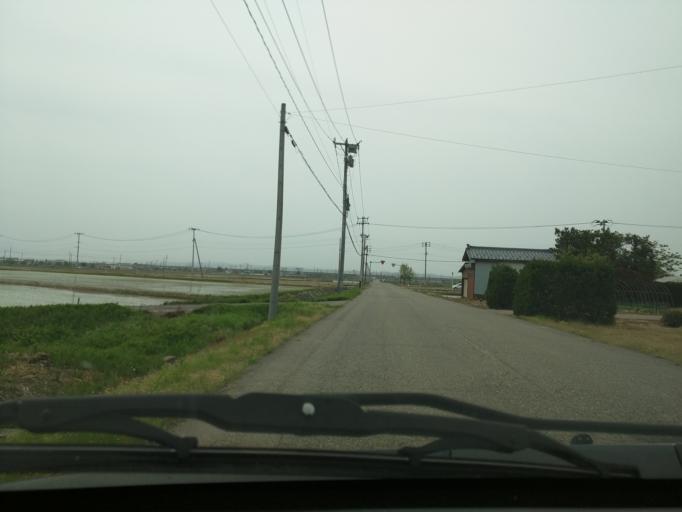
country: JP
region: Niigata
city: Mitsuke
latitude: 37.5511
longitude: 138.9076
